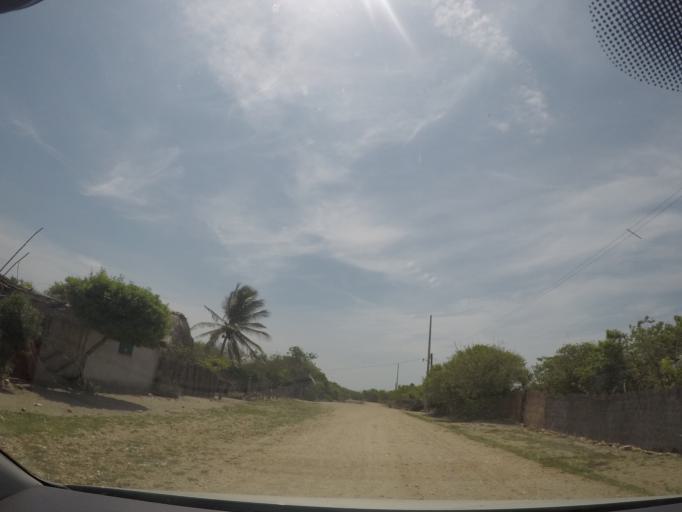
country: MX
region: Oaxaca
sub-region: Salina Cruz
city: Salina Cruz
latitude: 16.1910
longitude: -95.1165
